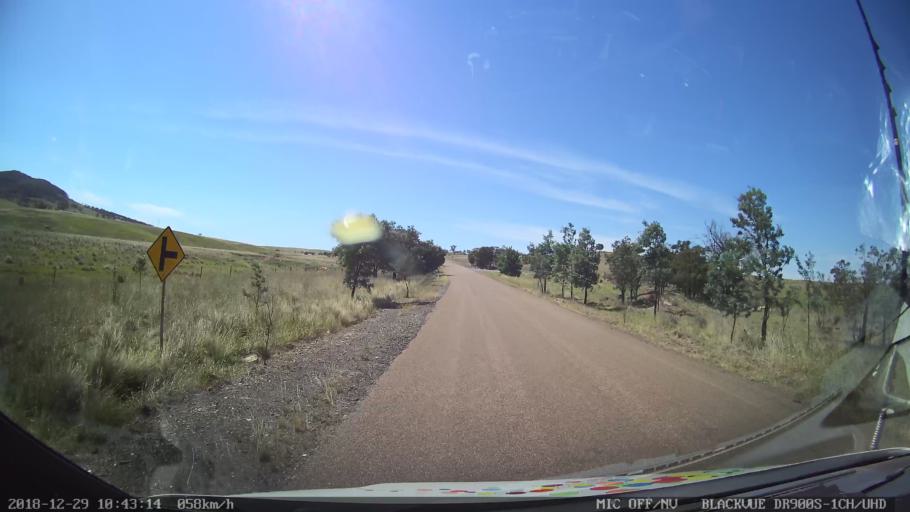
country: AU
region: New South Wales
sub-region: Palerang
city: Bungendore
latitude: -35.0395
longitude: 149.5364
